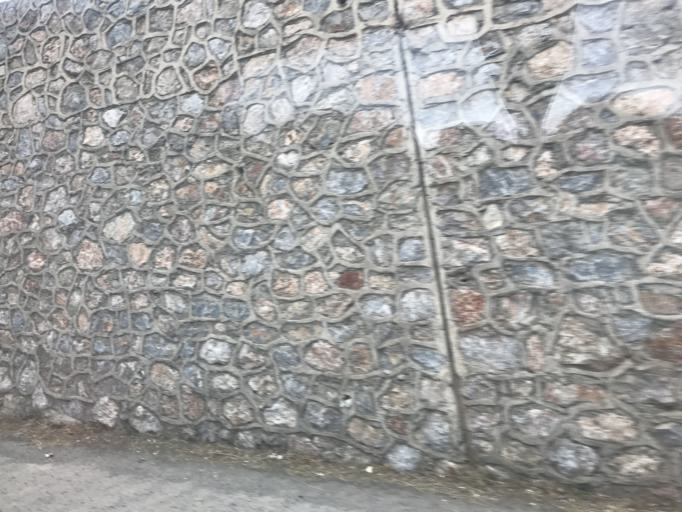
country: TR
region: Balikesir
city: Ivrindi
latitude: 39.6132
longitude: 27.5443
